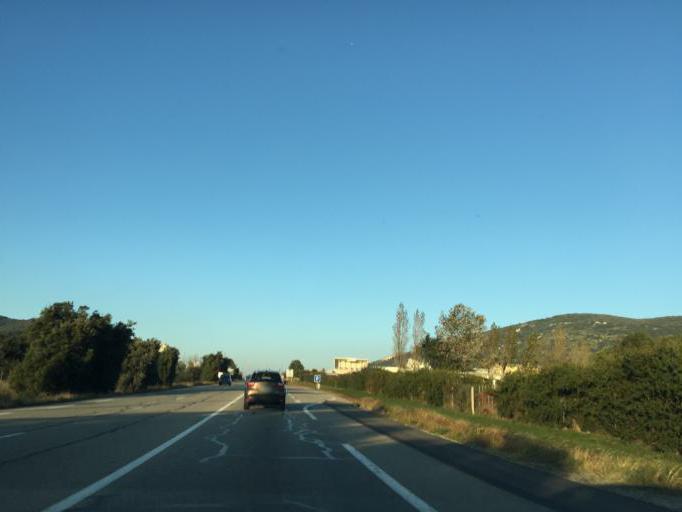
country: FR
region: Rhone-Alpes
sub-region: Departement de la Drome
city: Malataverne
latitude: 44.4586
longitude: 4.7550
